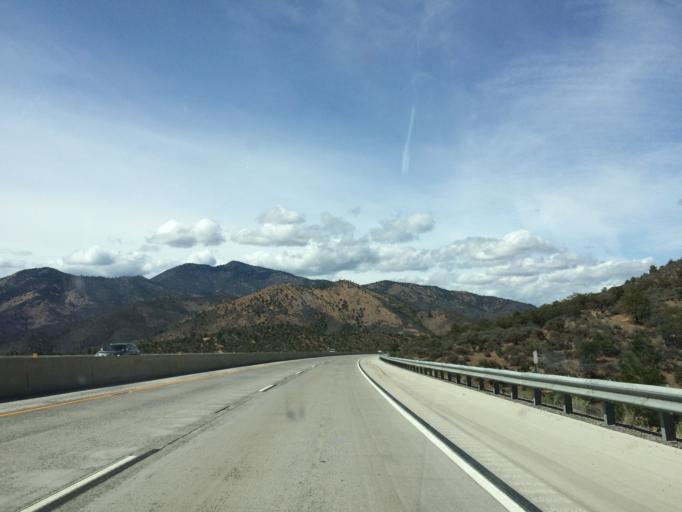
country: US
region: California
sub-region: Siskiyou County
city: Yreka
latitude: 41.8160
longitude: -122.5755
